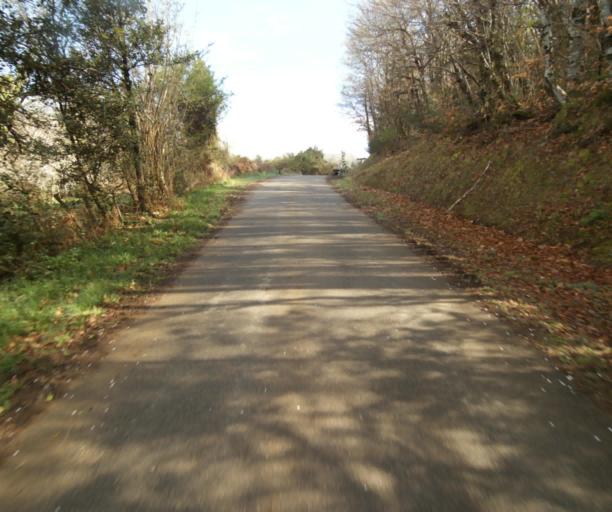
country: FR
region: Limousin
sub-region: Departement de la Correze
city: Laguenne
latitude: 45.2608
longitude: 1.8200
